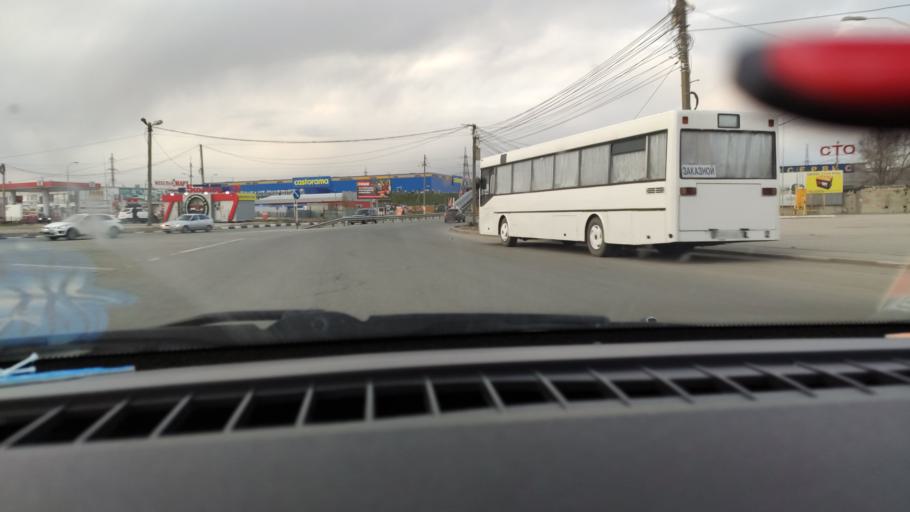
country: RU
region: Saratov
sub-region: Saratovskiy Rayon
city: Saratov
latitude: 51.6201
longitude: 45.9746
